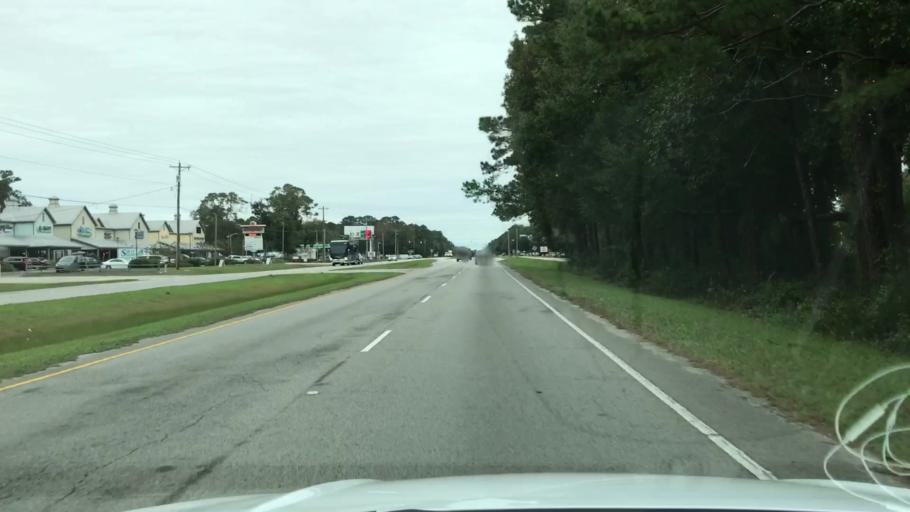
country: US
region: South Carolina
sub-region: Georgetown County
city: Murrells Inlet
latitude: 33.5338
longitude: -79.0590
